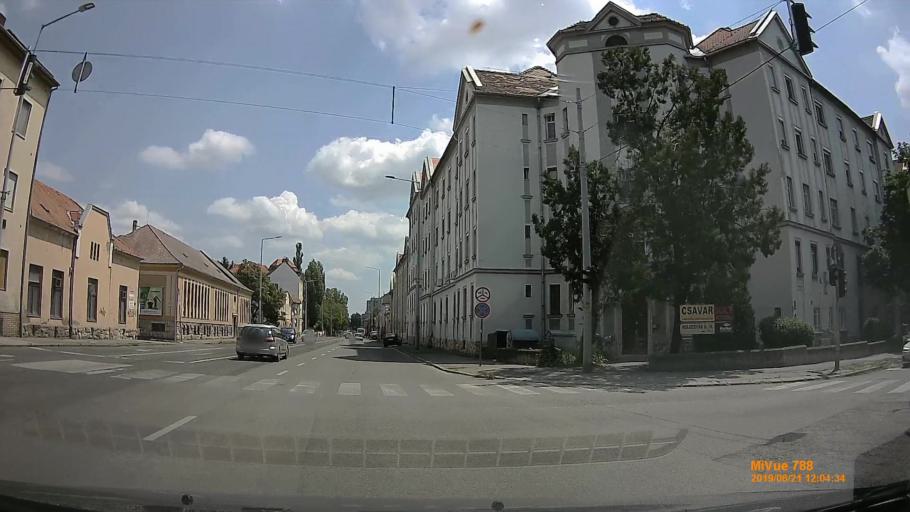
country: HU
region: Baranya
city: Pecs
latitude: 46.0710
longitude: 18.2172
